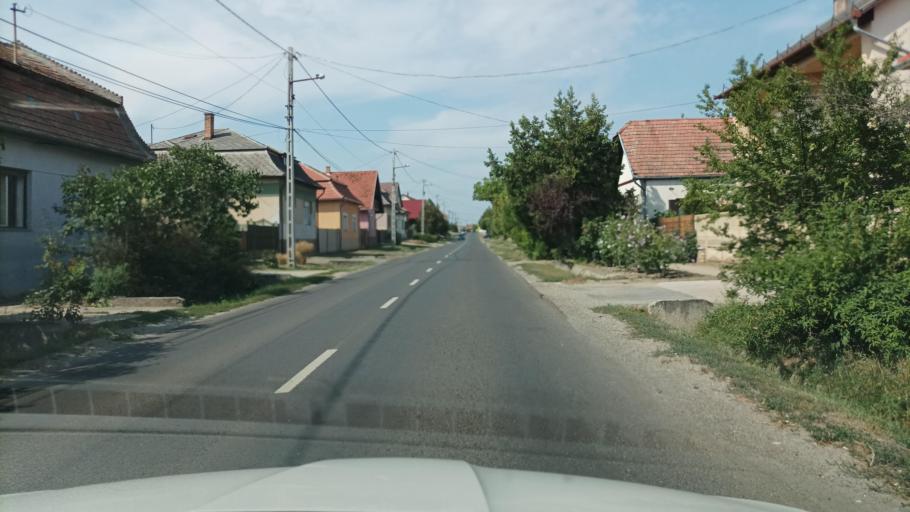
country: HU
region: Pest
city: Hevizgyoerk
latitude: 47.6269
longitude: 19.5244
